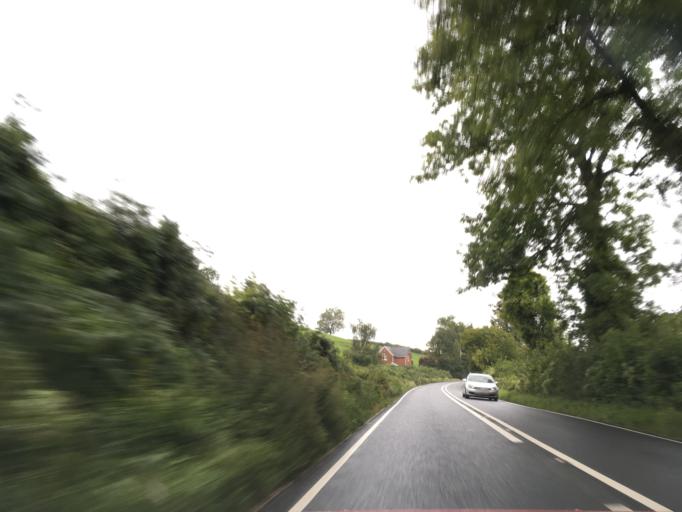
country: GB
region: England
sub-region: Gloucestershire
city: Mitcheldean
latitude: 51.8842
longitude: -2.4753
